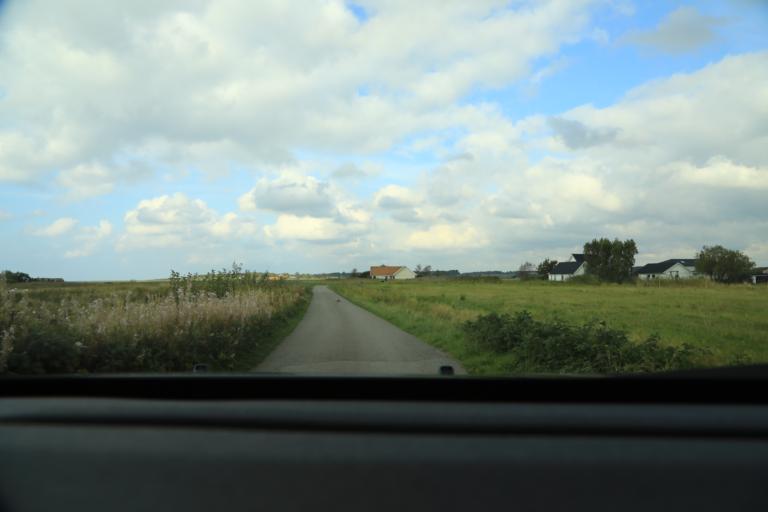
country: SE
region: Halland
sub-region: Varbergs Kommun
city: Traslovslage
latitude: 57.0286
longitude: 12.3242
